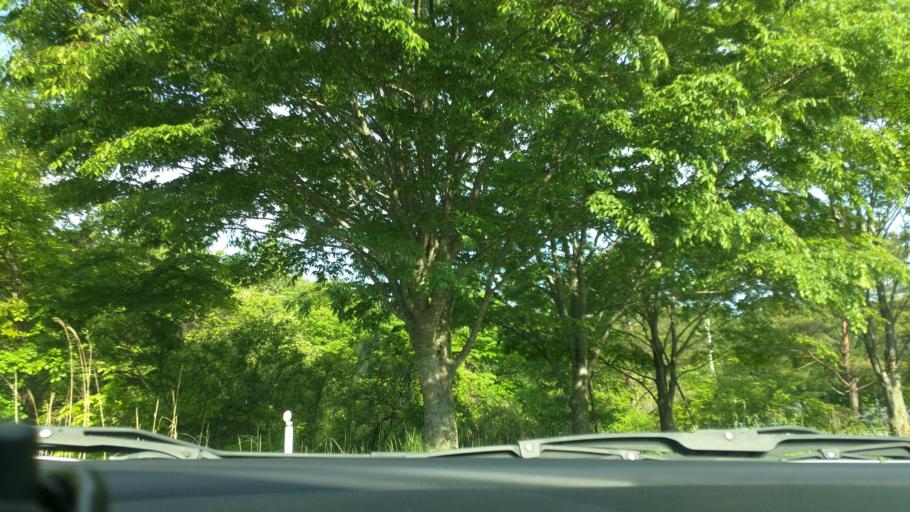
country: JP
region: Fukushima
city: Inawashiro
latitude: 37.2771
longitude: 140.0641
